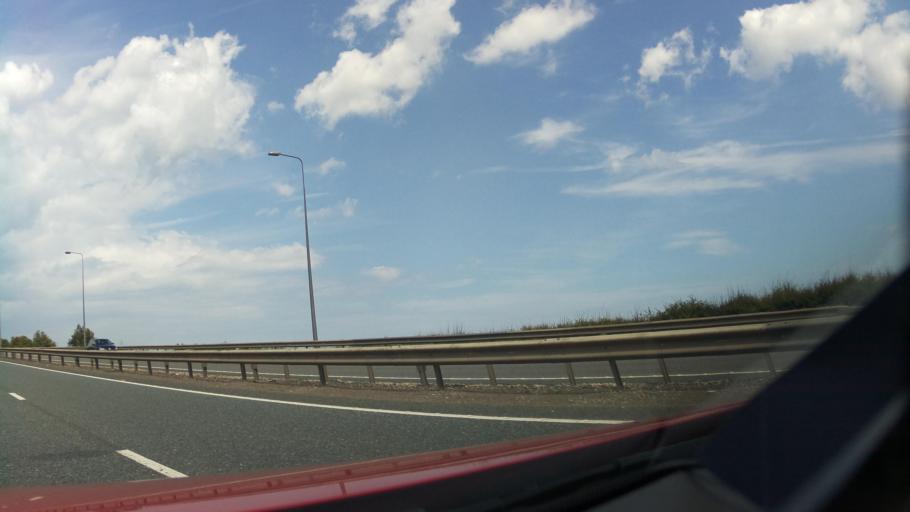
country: GB
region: England
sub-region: Hartlepool
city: Elwick
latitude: 54.6724
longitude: -1.2993
